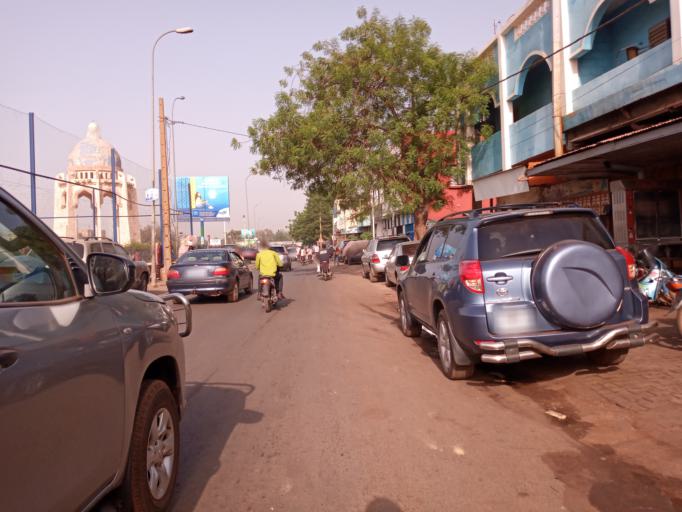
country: ML
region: Bamako
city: Bamako
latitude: 12.6513
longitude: -7.9923
